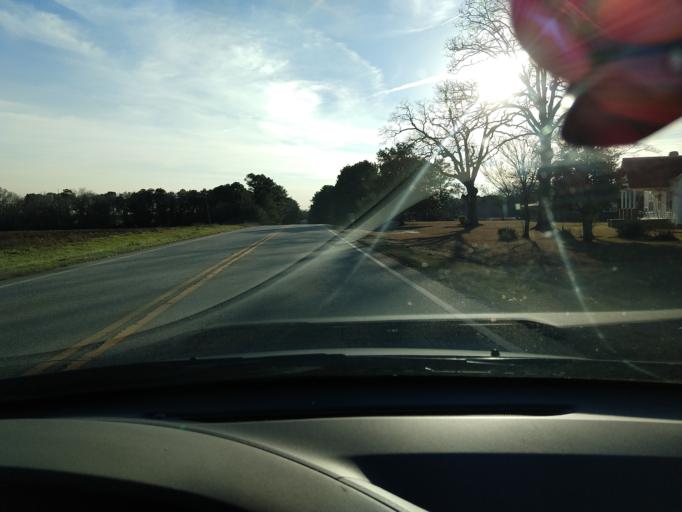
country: US
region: Georgia
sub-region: Sumter County
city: Americus
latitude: 32.1330
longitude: -84.1490
